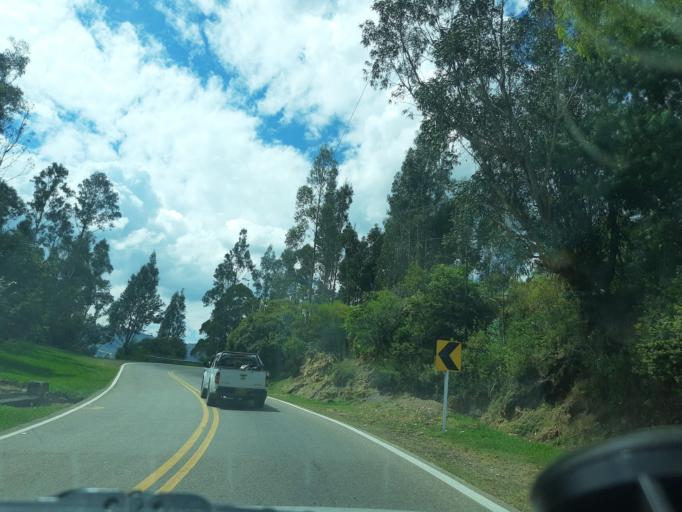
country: CO
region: Boyaca
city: Raquira
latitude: 5.5780
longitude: -73.6862
